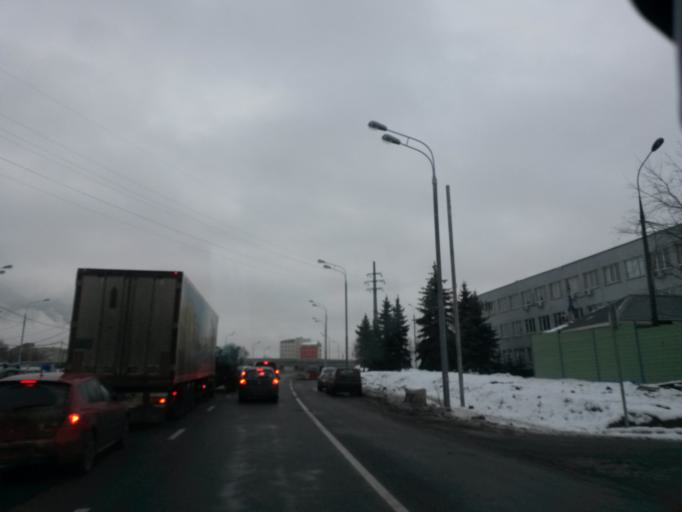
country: RU
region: Moskovskaya
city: Bol'shaya Setun'
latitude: 55.7048
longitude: 37.4169
